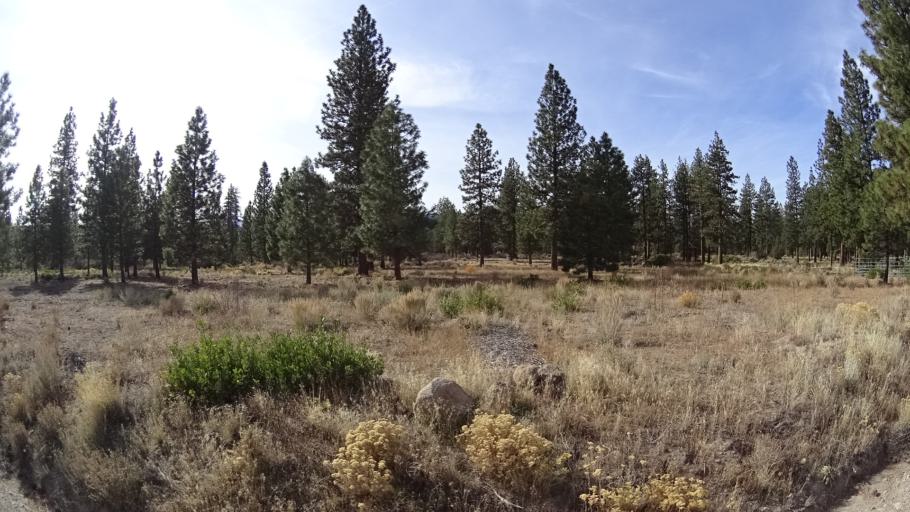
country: US
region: California
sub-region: Siskiyou County
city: Weed
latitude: 41.4912
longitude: -122.3722
